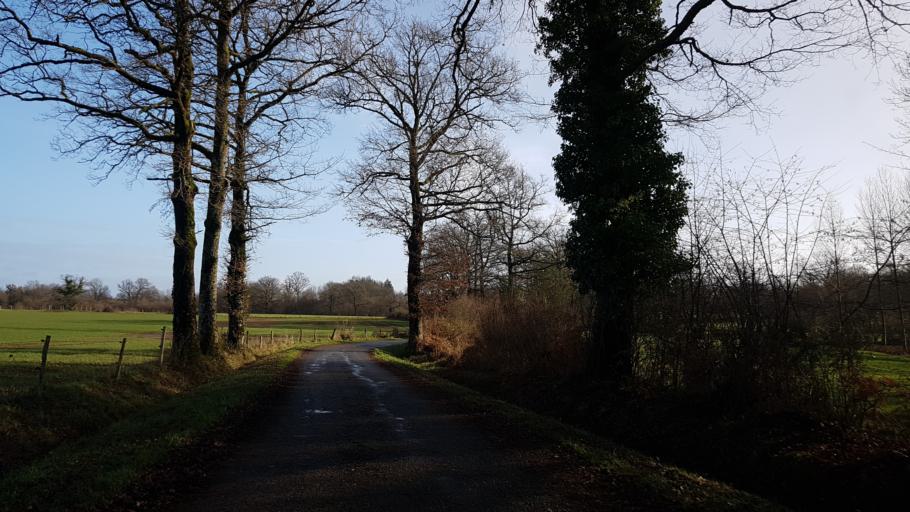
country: FR
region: Poitou-Charentes
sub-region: Departement de la Charente
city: Etagnac
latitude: 45.9245
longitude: 0.8111
